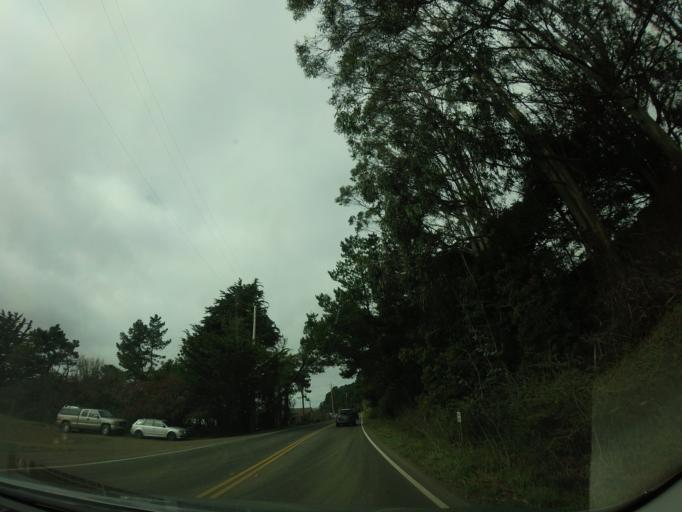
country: US
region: California
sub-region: Marin County
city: Inverness
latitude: 38.1412
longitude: -122.8737
